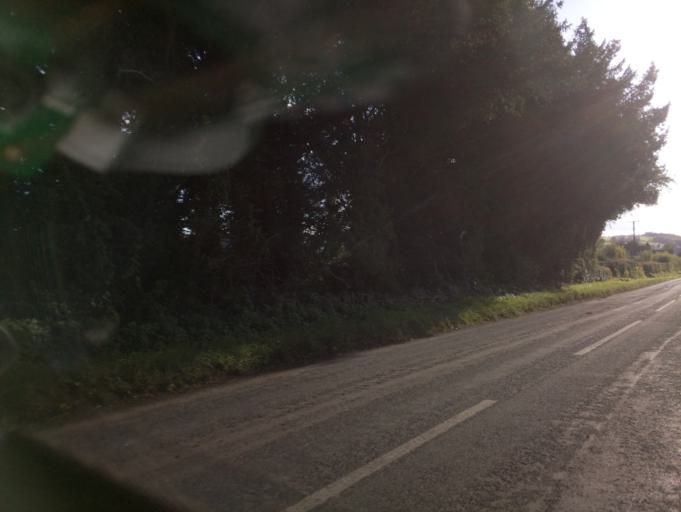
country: GB
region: Wales
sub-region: Sir Powys
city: Hay
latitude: 52.0811
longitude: -3.1209
